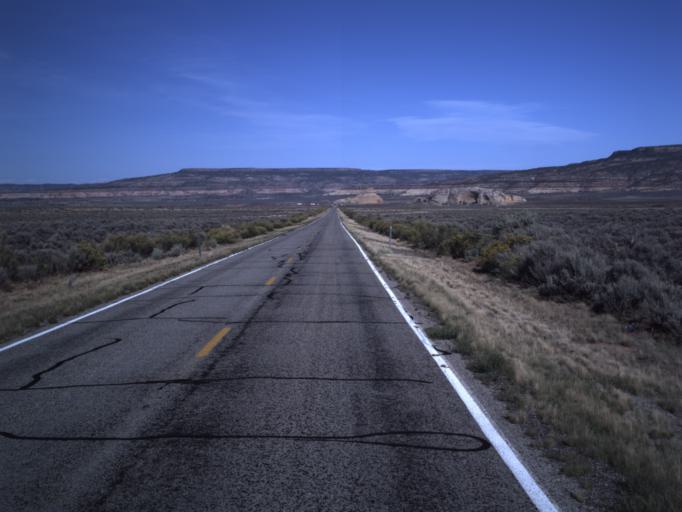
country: US
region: Utah
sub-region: San Juan County
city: Monticello
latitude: 38.0630
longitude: -109.3920
